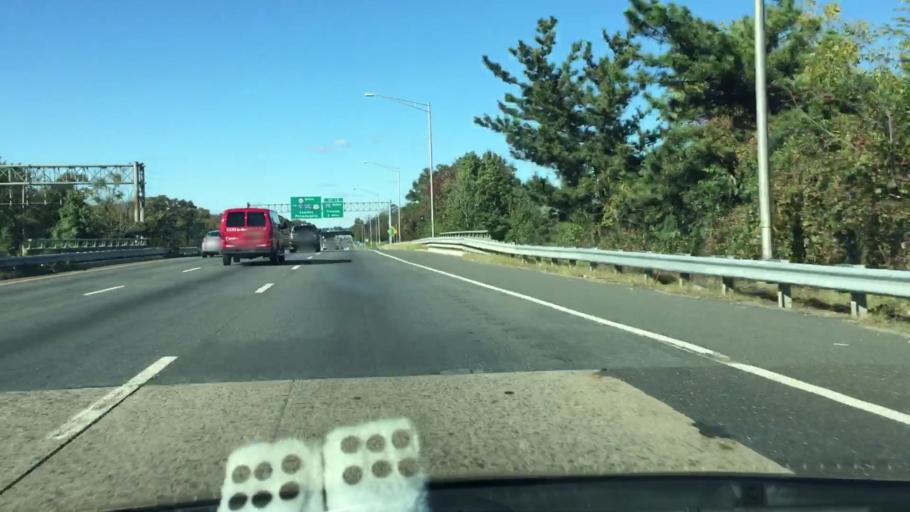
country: US
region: New Jersey
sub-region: Camden County
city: Glendora
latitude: 39.8365
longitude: -75.0915
